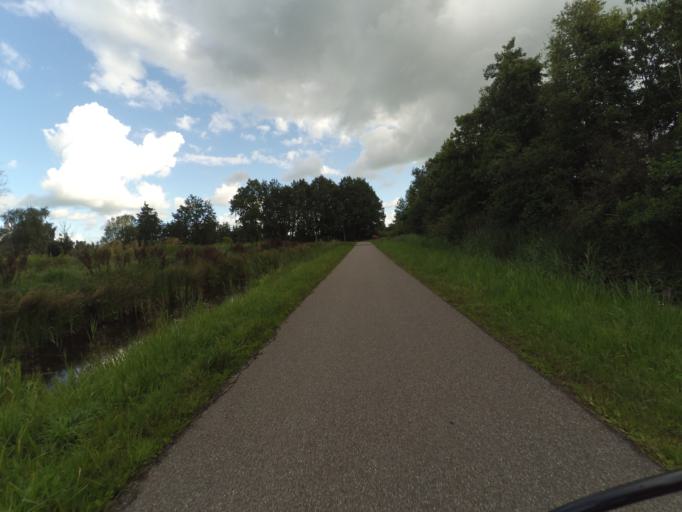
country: NL
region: Friesland
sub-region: Gemeente Dantumadiel
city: De Westereen
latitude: 53.2630
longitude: 6.0264
